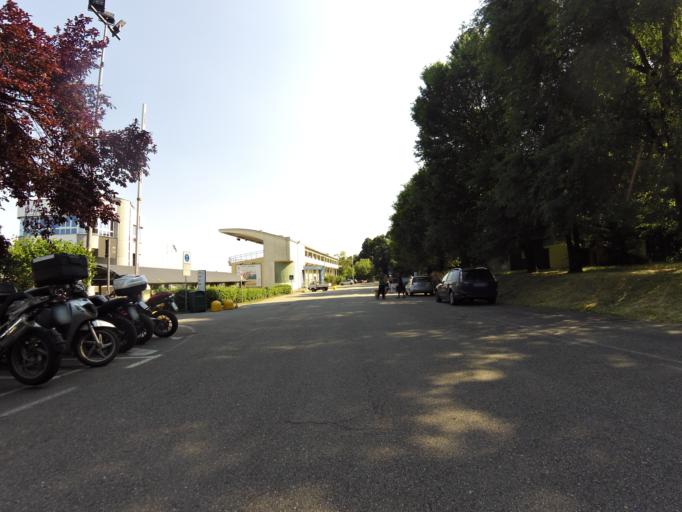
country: IT
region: Lombardy
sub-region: Citta metropolitana di Milano
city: Novegro-Tregarezzo-San Felice
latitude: 45.4739
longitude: 9.2887
